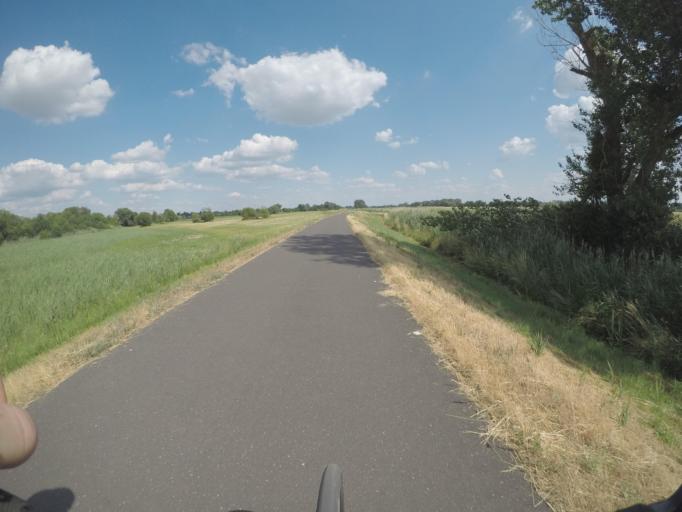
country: DE
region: Brandenburg
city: Ketzin
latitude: 52.4656
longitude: 12.8413
